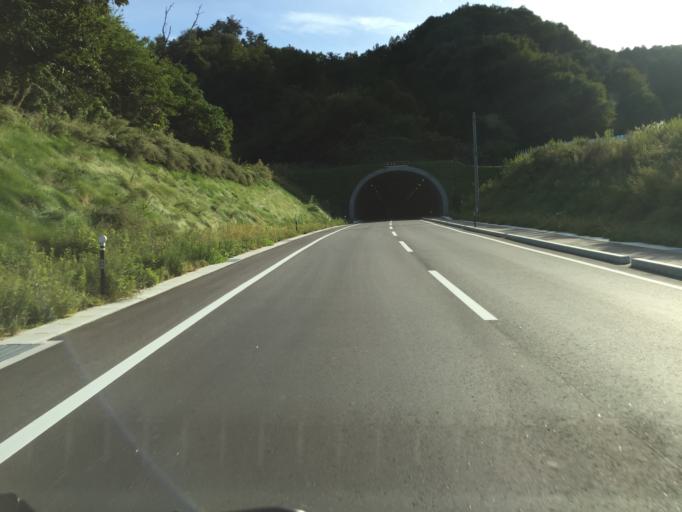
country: JP
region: Fukushima
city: Hobaramachi
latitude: 37.7392
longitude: 140.6072
